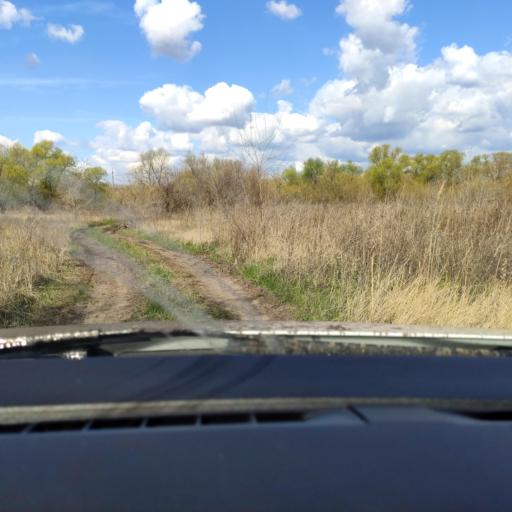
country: RU
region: Voronezj
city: Pridonskoy
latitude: 51.6962
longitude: 39.0541
